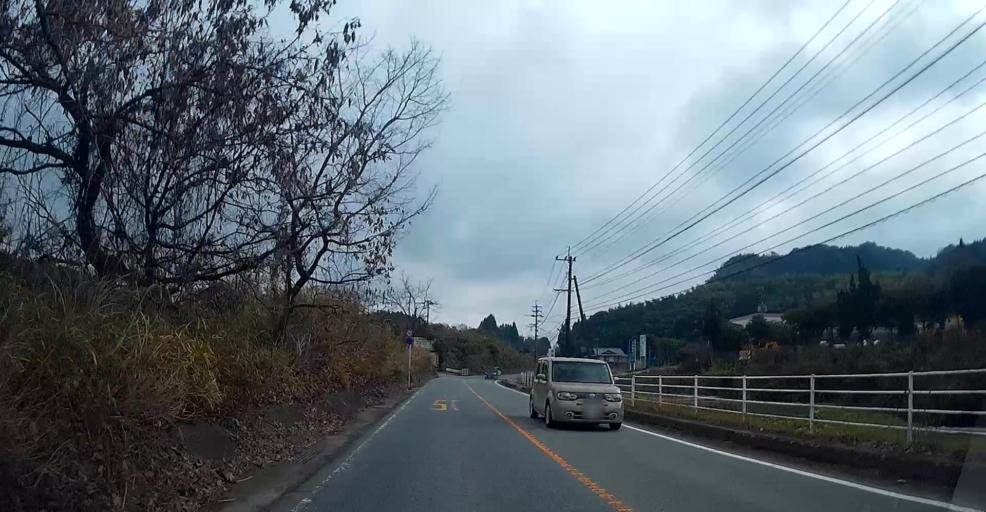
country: JP
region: Kumamoto
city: Matsubase
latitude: 32.6464
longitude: 130.7273
